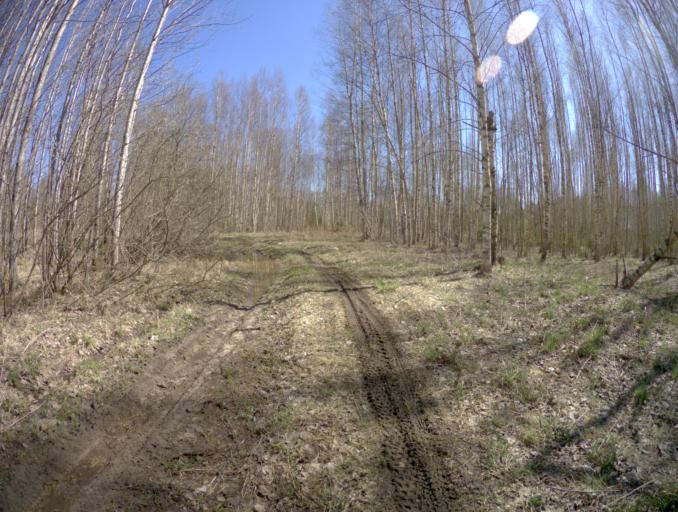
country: RU
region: Vladimir
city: Ivanishchi
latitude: 55.8623
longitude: 40.4173
